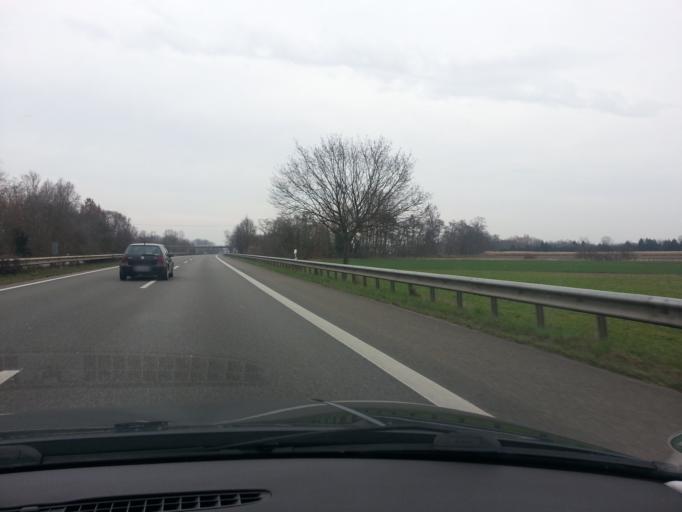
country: DE
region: Rheinland-Pfalz
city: Neuhofen
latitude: 49.4082
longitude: 8.4104
